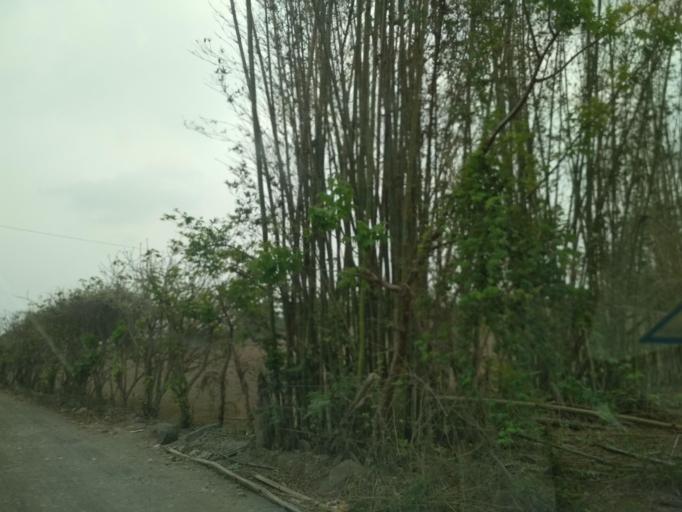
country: MX
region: Veracruz
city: Paso del Toro
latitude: 19.0281
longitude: -96.1488
